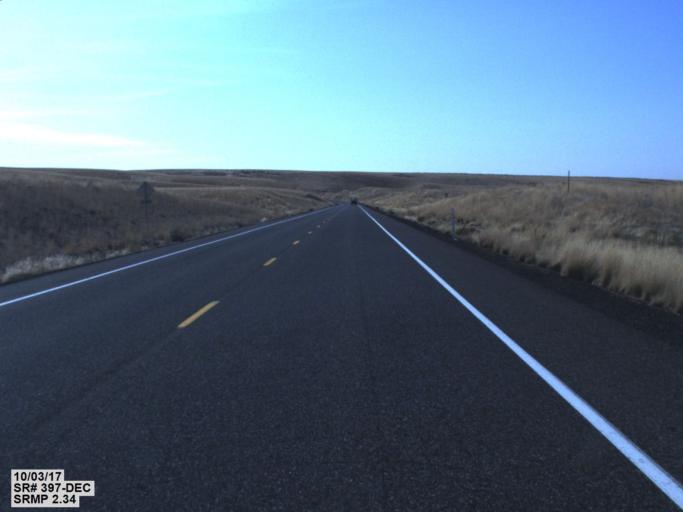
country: US
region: Washington
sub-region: Benton County
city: Highland
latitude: 46.1546
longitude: -119.1589
